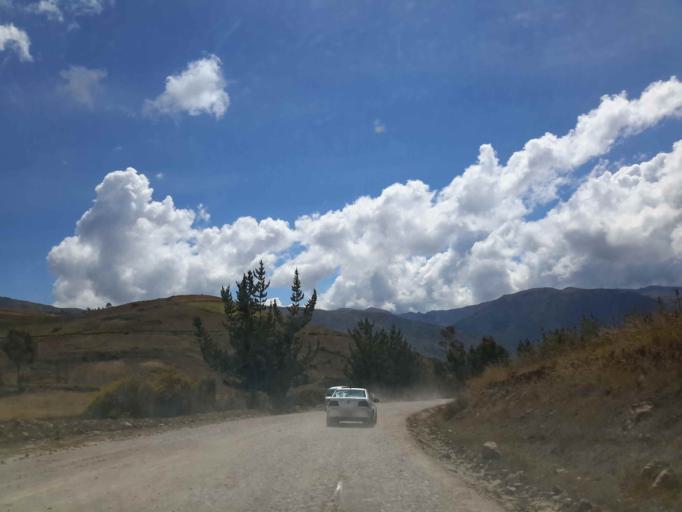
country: PE
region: Apurimac
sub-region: Provincia de Andahuaylas
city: Pacucha
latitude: -13.6311
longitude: -73.3386
